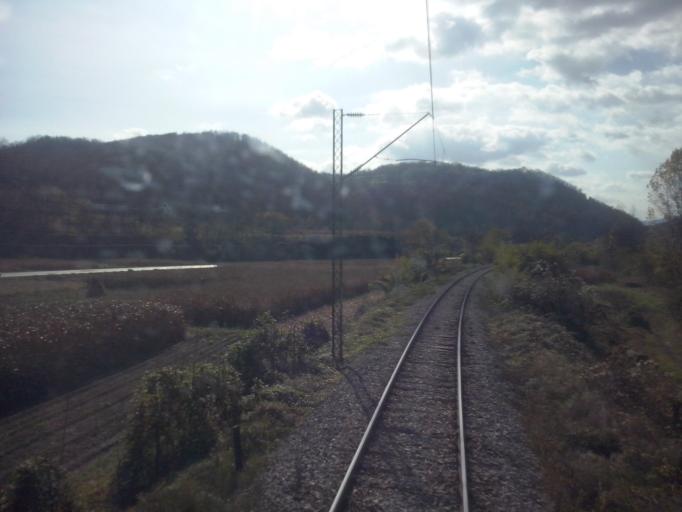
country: RS
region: Central Serbia
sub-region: Zlatiborski Okrug
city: Pozega
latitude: 43.9067
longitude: 20.0021
